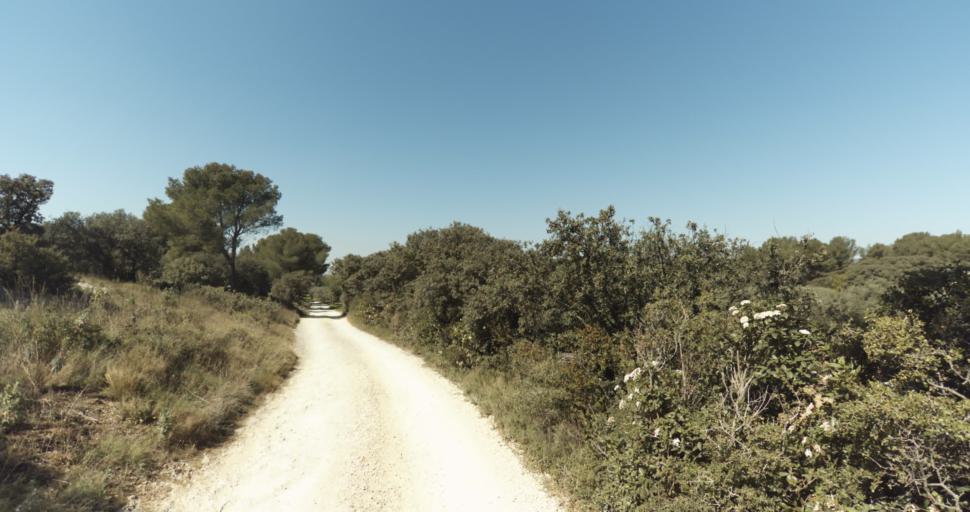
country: FR
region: Provence-Alpes-Cote d'Azur
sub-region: Departement des Bouches-du-Rhone
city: Pelissanne
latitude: 43.6222
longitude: 5.1668
